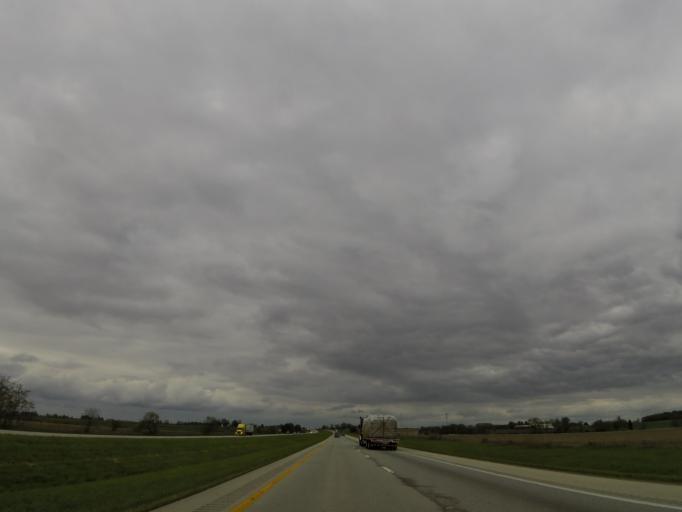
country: US
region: Ohio
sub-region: Greene County
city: Jamestown
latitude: 39.5501
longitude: -83.7387
